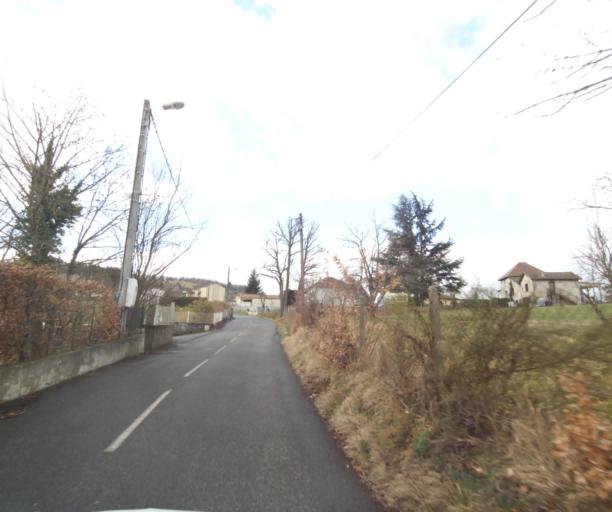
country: FR
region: Rhone-Alpes
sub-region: Departement de la Loire
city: Sorbiers
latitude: 45.4717
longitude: 4.4484
